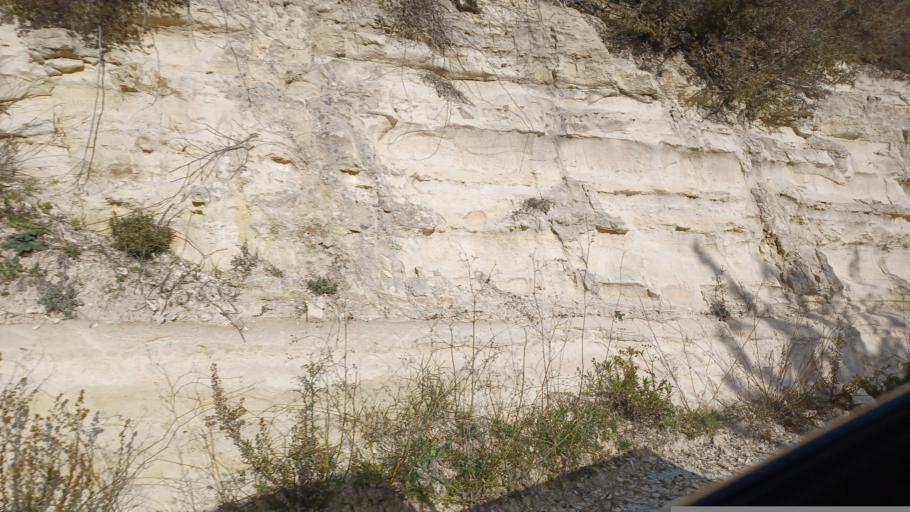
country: CY
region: Limassol
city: Pachna
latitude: 34.8300
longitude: 32.7815
